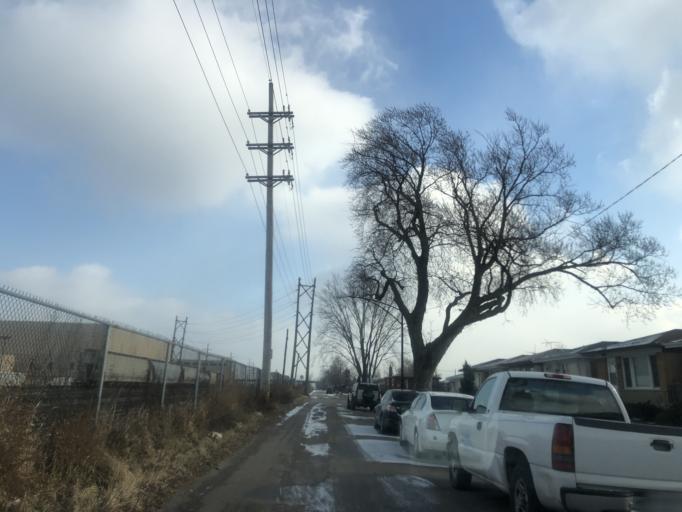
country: US
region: Illinois
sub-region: Cook County
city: Hometown
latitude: 41.7569
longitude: -87.7109
